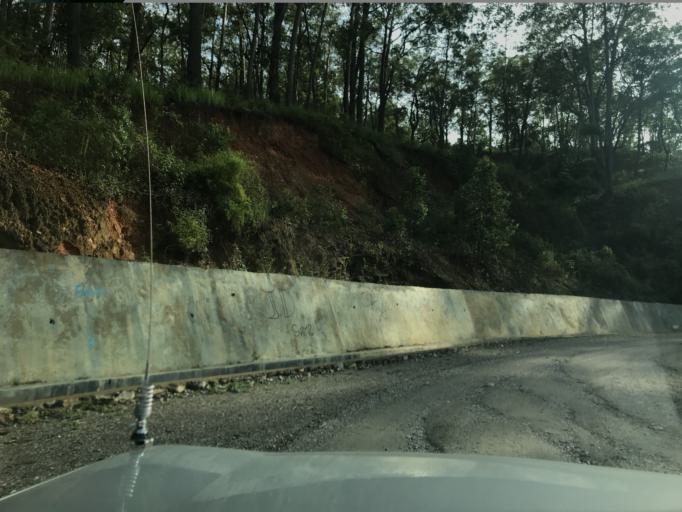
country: TL
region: Aileu
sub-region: Aileu Villa
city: Aileu
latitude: -8.6631
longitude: 125.5342
